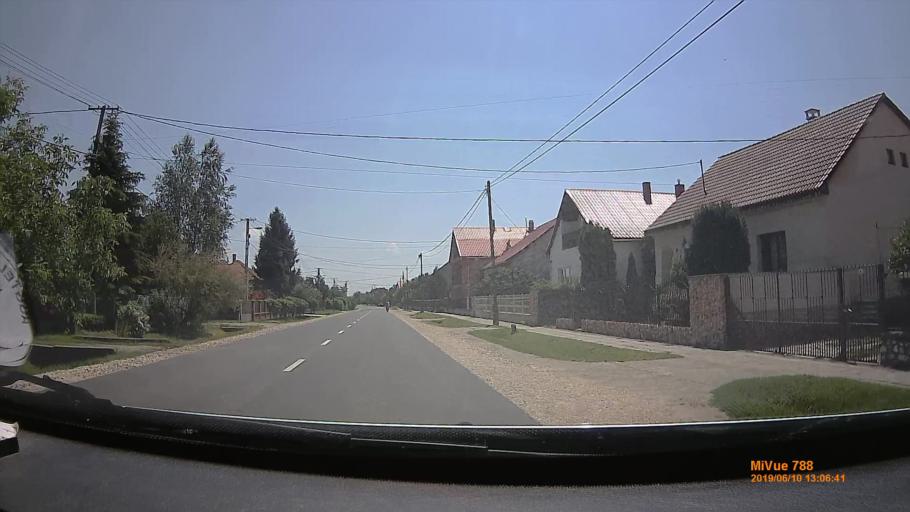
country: HU
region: Borsod-Abauj-Zemplen
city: Gesztely
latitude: 48.0930
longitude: 20.9668
